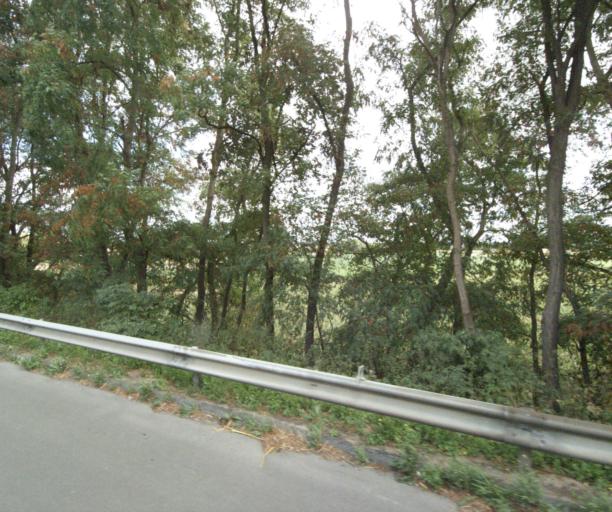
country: FR
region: Nord-Pas-de-Calais
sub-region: Departement du Nord
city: Genech
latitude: 50.4981
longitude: 3.2122
